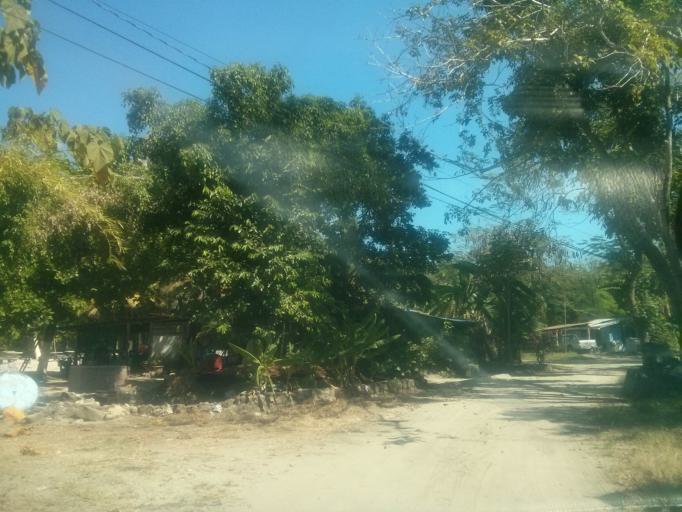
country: CR
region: Puntarenas
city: Paquera
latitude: 9.6096
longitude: -85.1448
